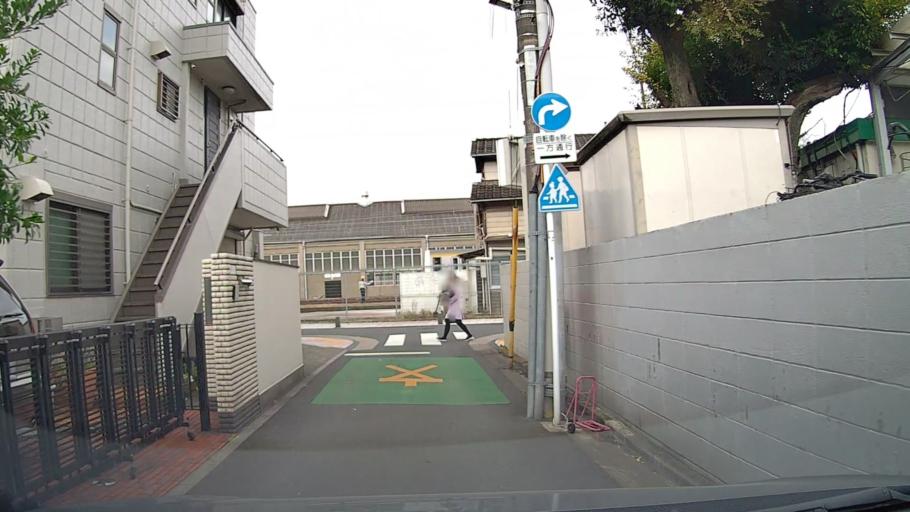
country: JP
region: Tokyo
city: Tokyo
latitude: 35.7047
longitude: 139.6703
